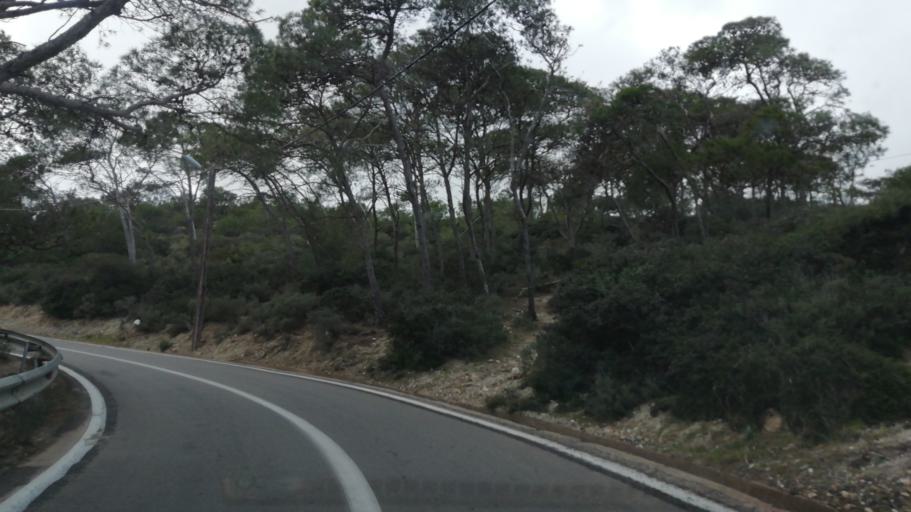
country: DZ
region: Oran
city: Oran
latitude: 35.7032
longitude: -0.6755
